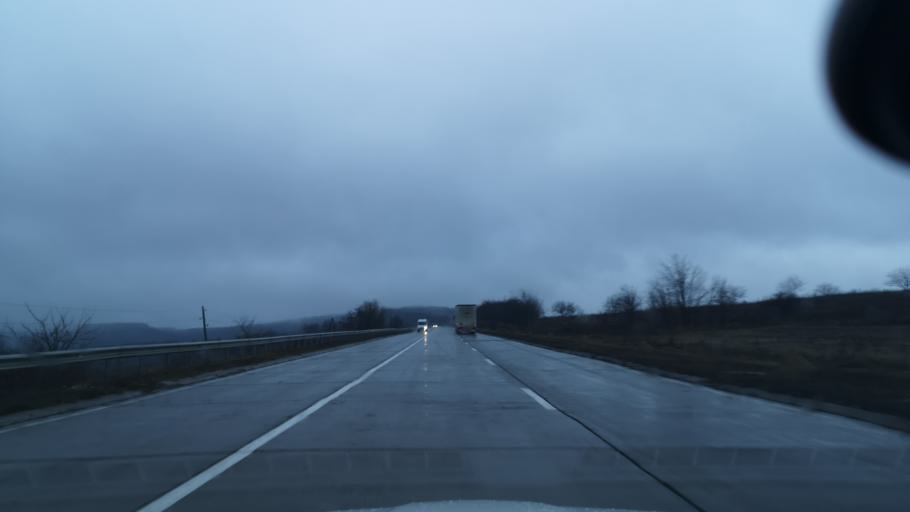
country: MD
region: Taraclia
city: Telenesti
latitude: 47.3615
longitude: 28.4546
